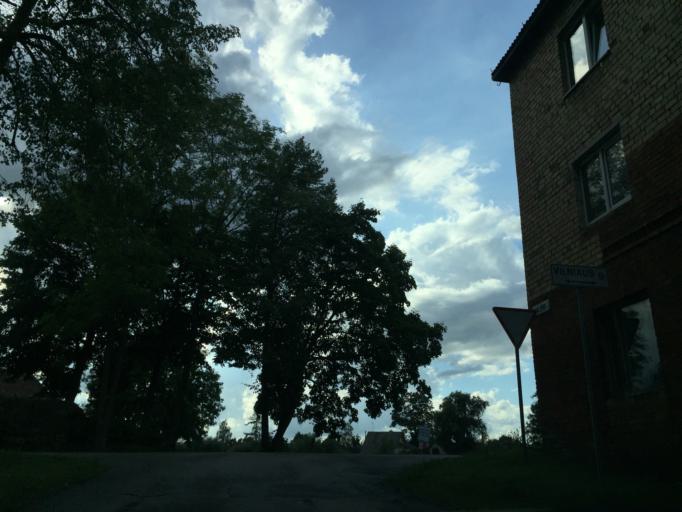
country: LT
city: Zagare
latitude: 56.3638
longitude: 23.2629
